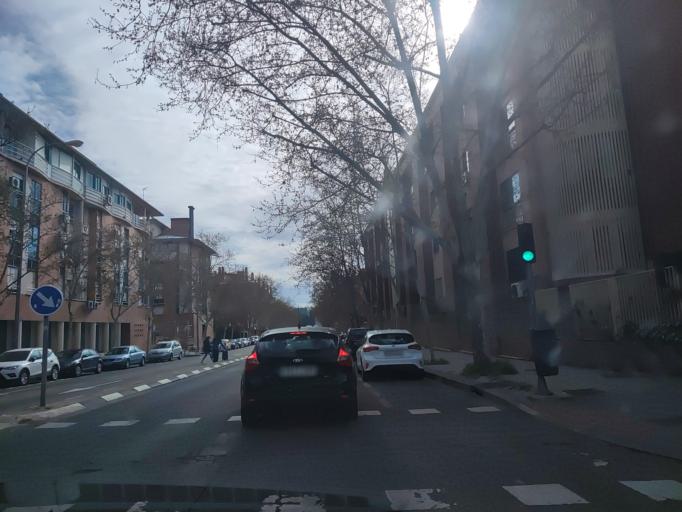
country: ES
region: Madrid
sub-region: Provincia de Madrid
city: Hortaleza
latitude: 40.4626
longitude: -3.6280
